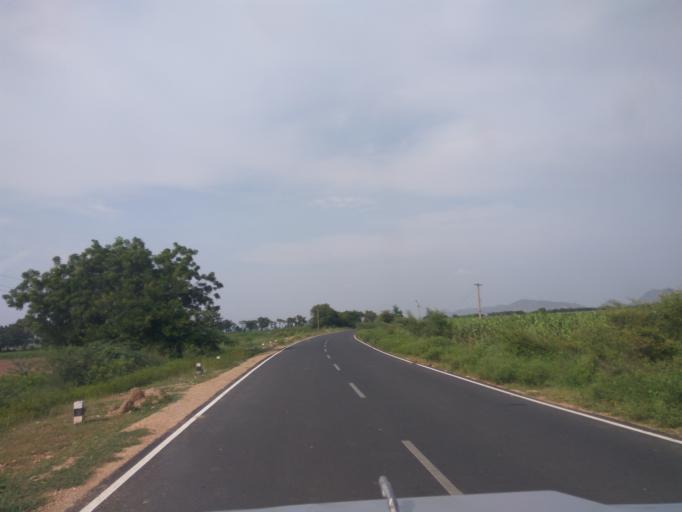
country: IN
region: Andhra Pradesh
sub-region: Prakasam
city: Markapur
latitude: 15.7741
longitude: 79.2422
